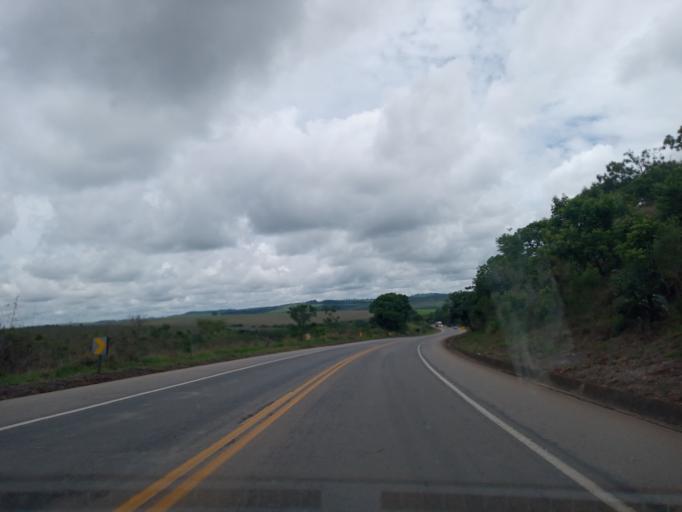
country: BR
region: Minas Gerais
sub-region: Ibia
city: Ibia
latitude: -19.5769
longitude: -46.6368
